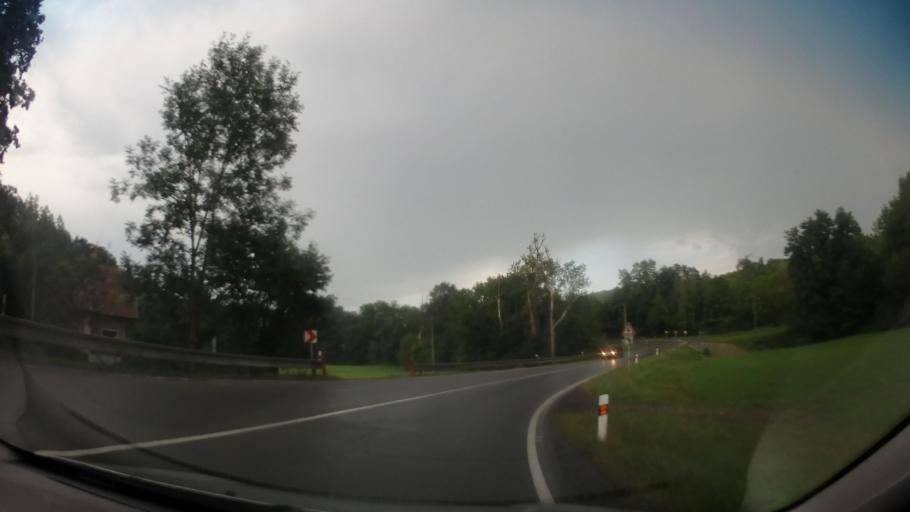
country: CZ
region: Olomoucky
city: Bila Lhota
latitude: 49.7047
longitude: 16.9960
